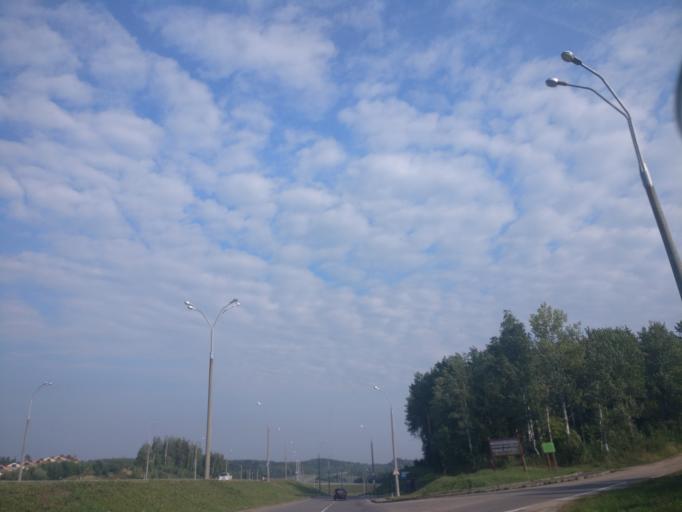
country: BY
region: Minsk
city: Lahoysk
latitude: 54.1758
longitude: 27.8197
